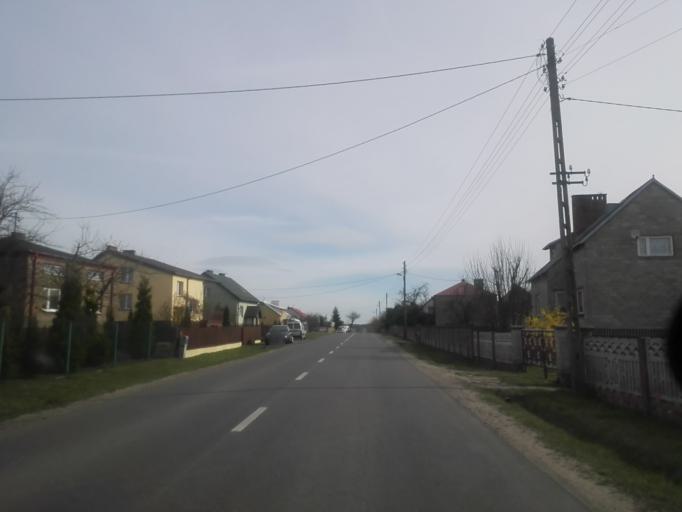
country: PL
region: Silesian Voivodeship
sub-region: Powiat czestochowski
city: Olsztyn
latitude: 50.7379
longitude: 19.3299
